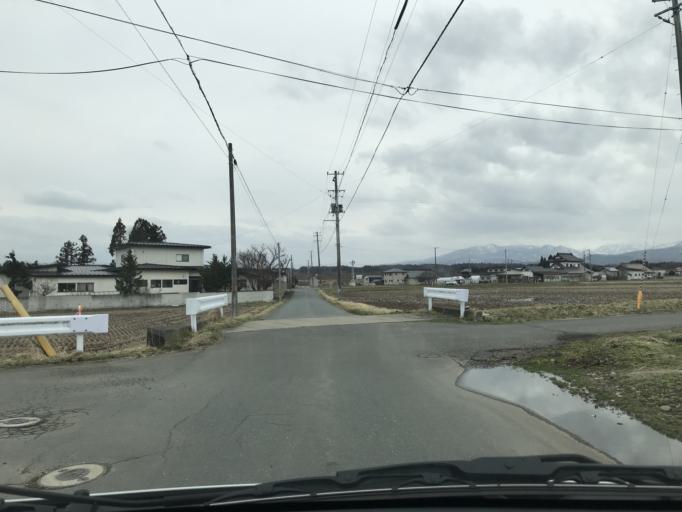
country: JP
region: Iwate
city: Kitakami
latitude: 39.2933
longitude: 141.0474
